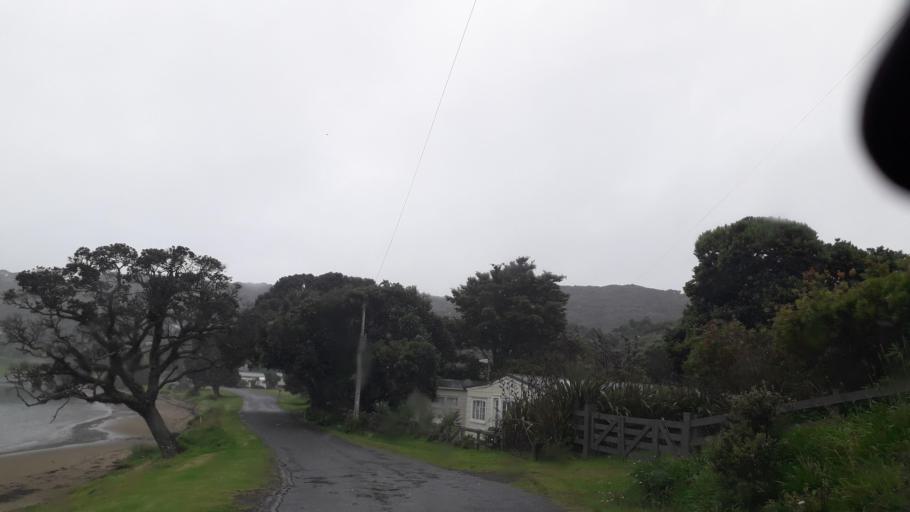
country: NZ
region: Northland
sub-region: Far North District
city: Paihia
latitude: -35.2268
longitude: 174.2637
